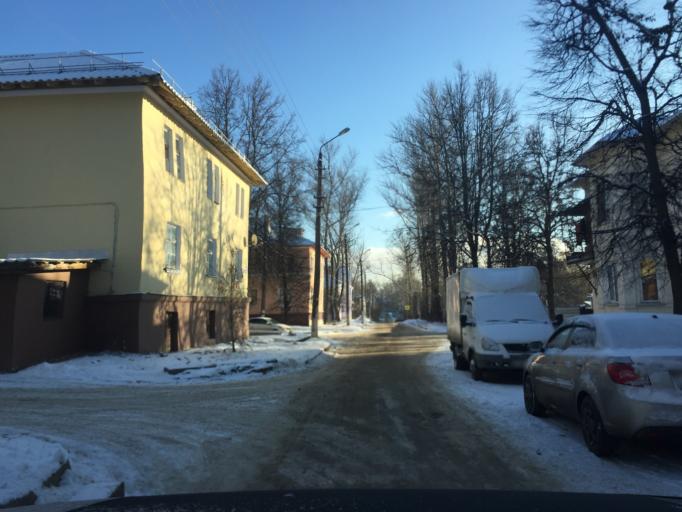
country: RU
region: Tula
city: Tula
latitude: 54.1836
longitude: 37.6978
